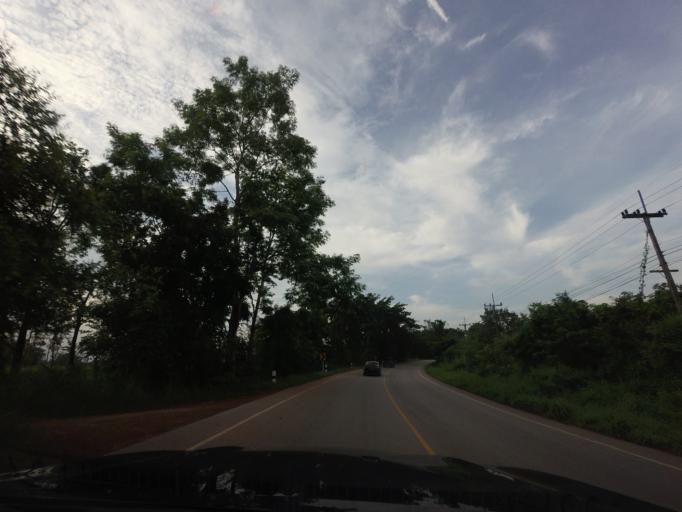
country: TH
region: Changwat Udon Thani
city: Nam Som
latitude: 17.8428
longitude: 102.2557
